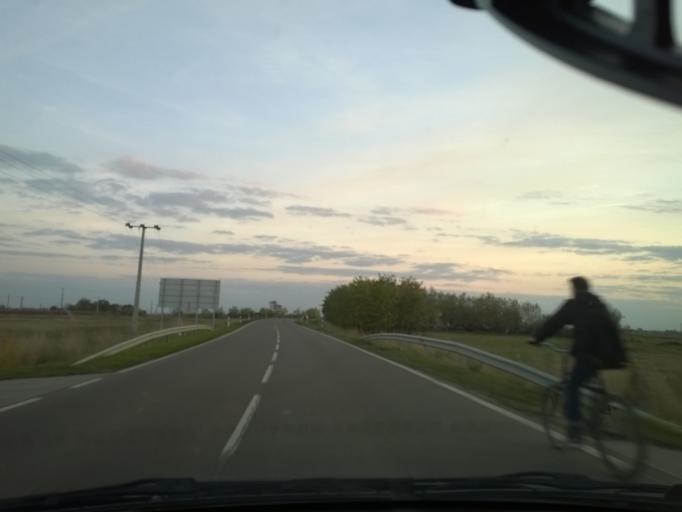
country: HU
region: Csongrad
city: Csongrad
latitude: 46.7151
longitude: 20.1140
